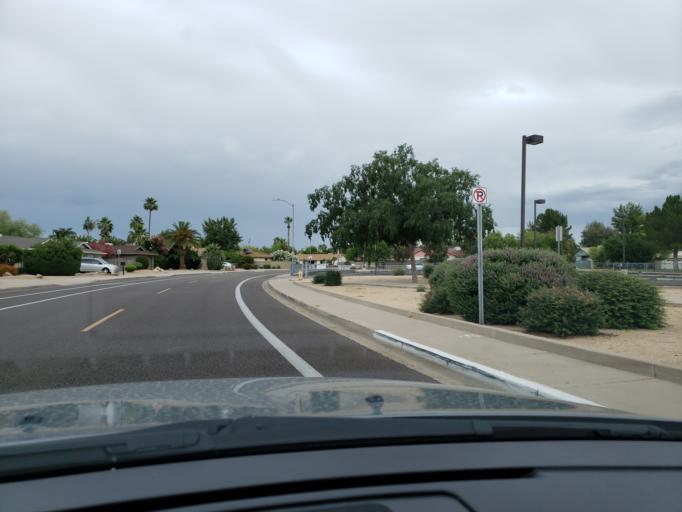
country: US
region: Arizona
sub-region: Maricopa County
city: Paradise Valley
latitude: 33.6207
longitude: -111.9532
